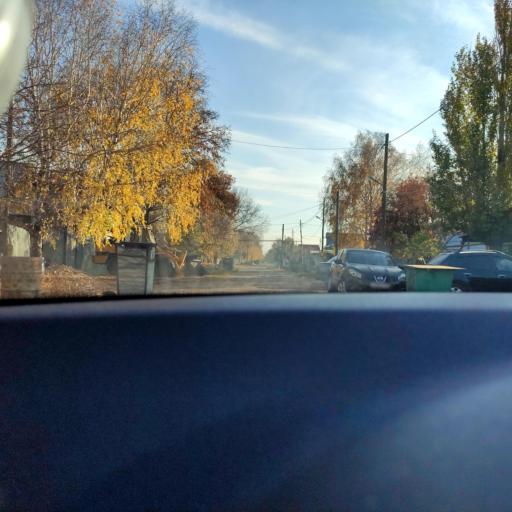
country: RU
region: Samara
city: Petra-Dubrava
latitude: 53.2569
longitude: 50.3245
